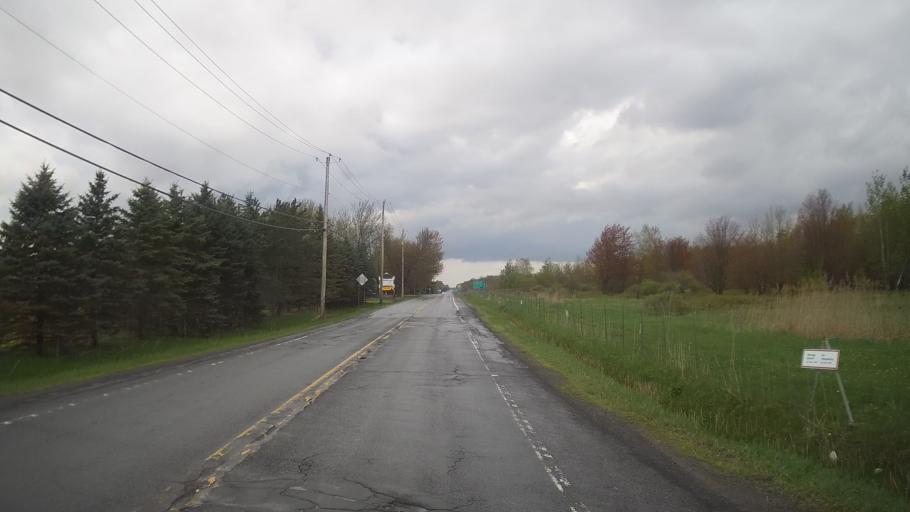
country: CA
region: Quebec
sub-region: Monteregie
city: Farnham
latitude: 45.2905
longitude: -73.0176
